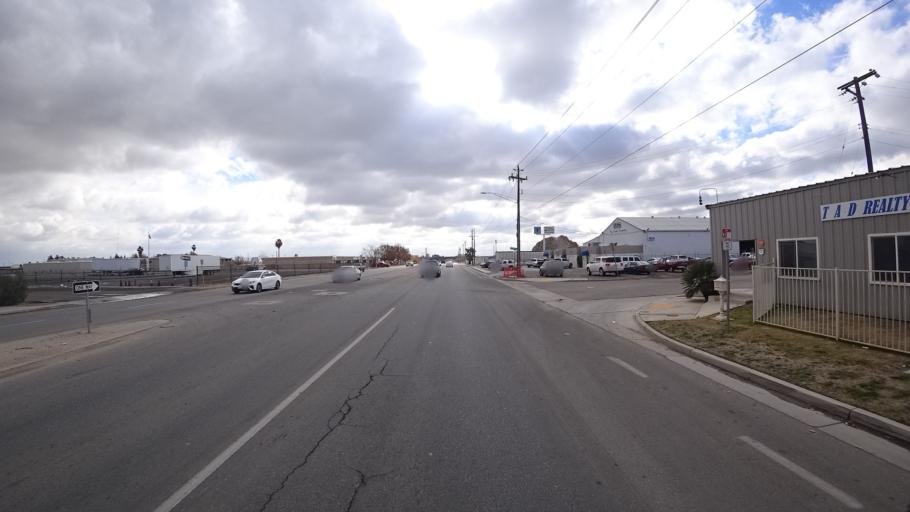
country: US
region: California
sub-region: Kern County
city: Bakersfield
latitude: 35.3578
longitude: -118.9676
